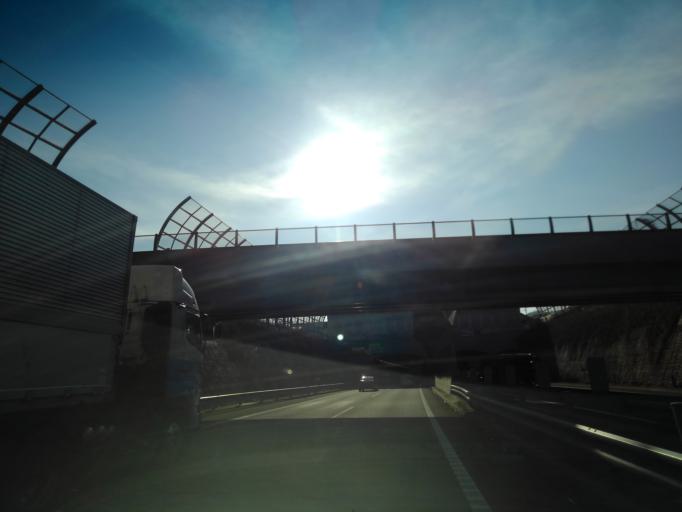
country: JP
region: Tokyo
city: Hachioji
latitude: 35.5915
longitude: 139.2865
